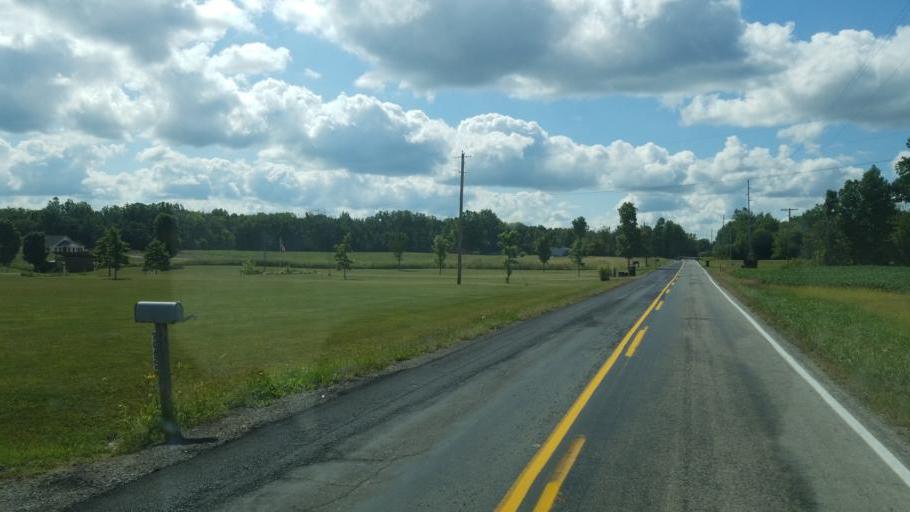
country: US
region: Ohio
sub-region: Lorain County
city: Lagrange
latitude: 41.1825
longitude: -82.1086
